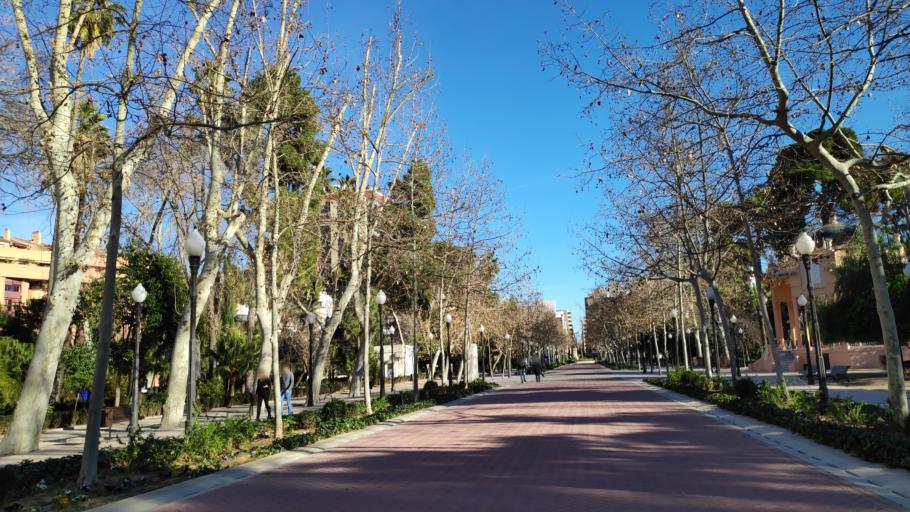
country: ES
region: Valencia
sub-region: Provincia de Castello
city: Castello de la Plana
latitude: 39.9884
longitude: -0.0456
